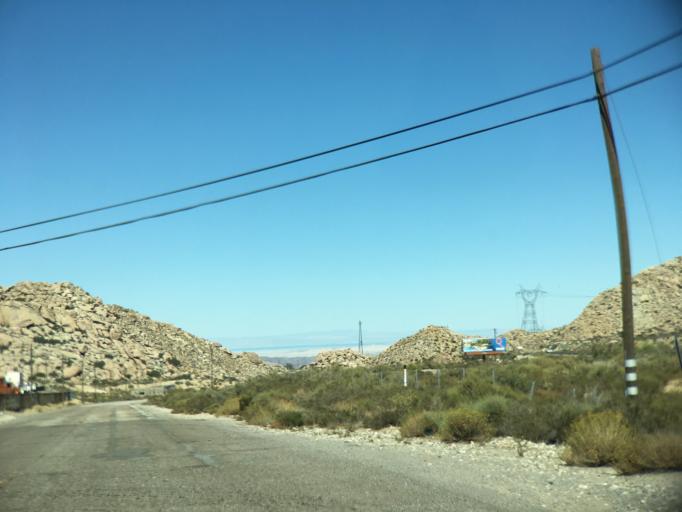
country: MX
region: Baja California
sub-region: Tecate
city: Cereso del Hongo
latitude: 32.6474
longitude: -116.1056
